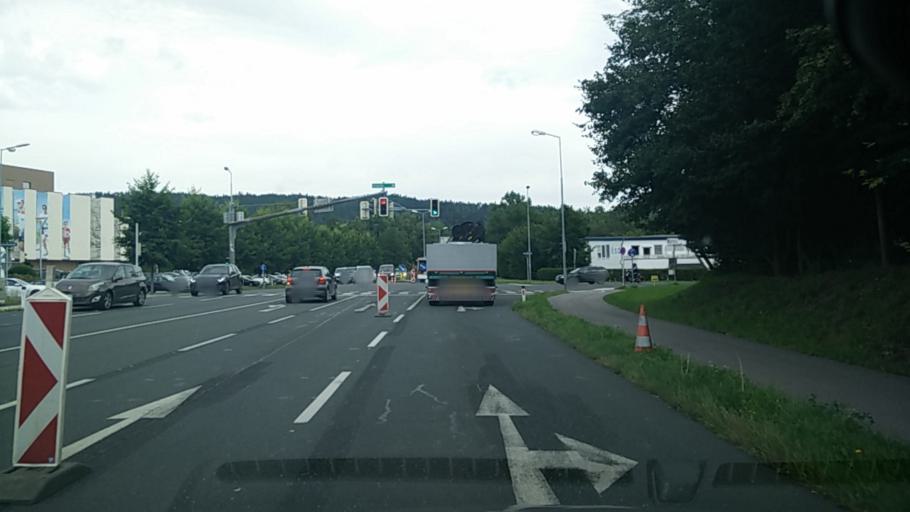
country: AT
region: Carinthia
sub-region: Klagenfurt am Woerthersee
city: Klagenfurt am Woerthersee
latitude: 46.6168
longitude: 14.2616
